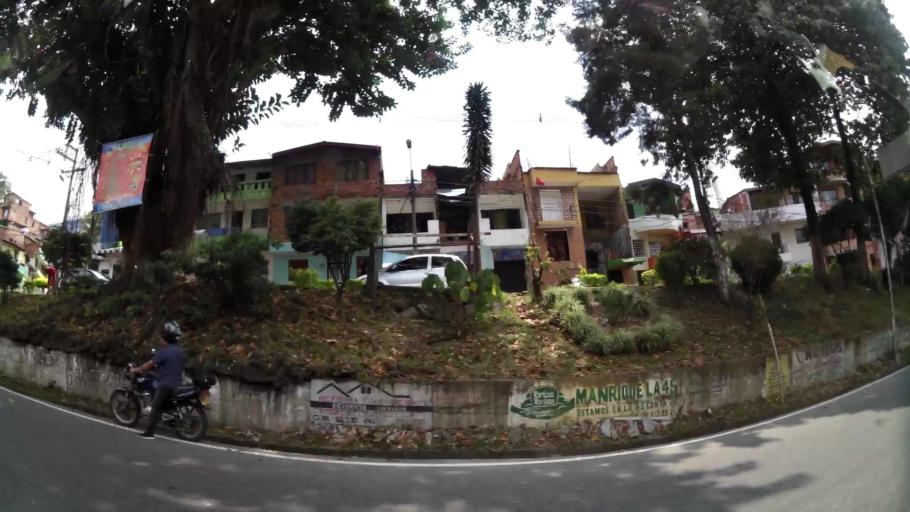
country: CO
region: Antioquia
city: Medellin
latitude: 6.2650
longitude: -75.5513
